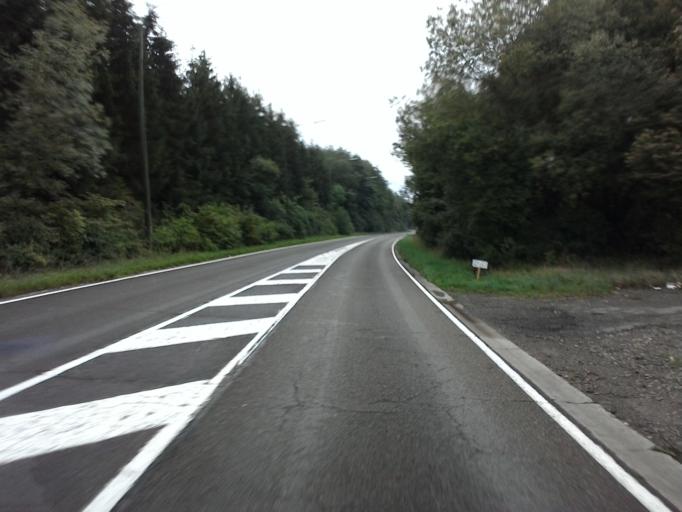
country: BE
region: Wallonia
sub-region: Province du Luxembourg
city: Arlon
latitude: 49.6646
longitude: 5.7719
